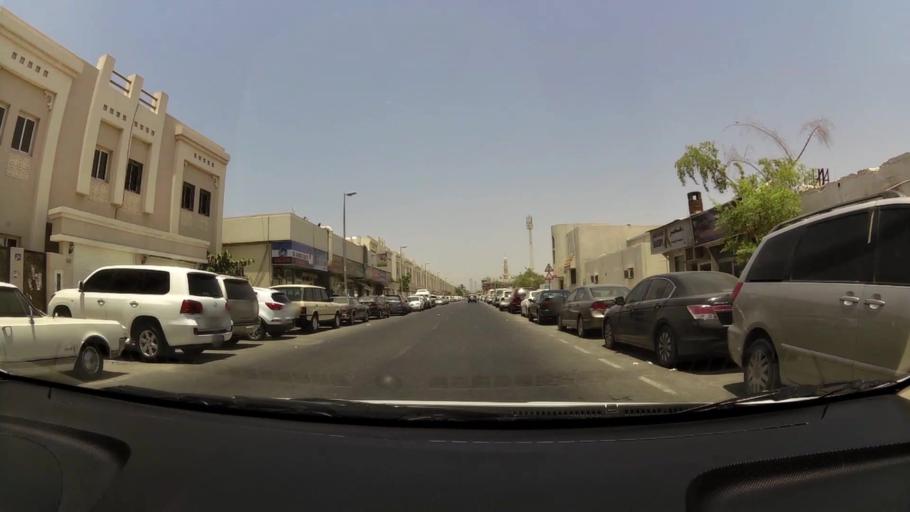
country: AE
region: Ash Shariqah
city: Sharjah
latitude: 25.2893
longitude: 55.3263
